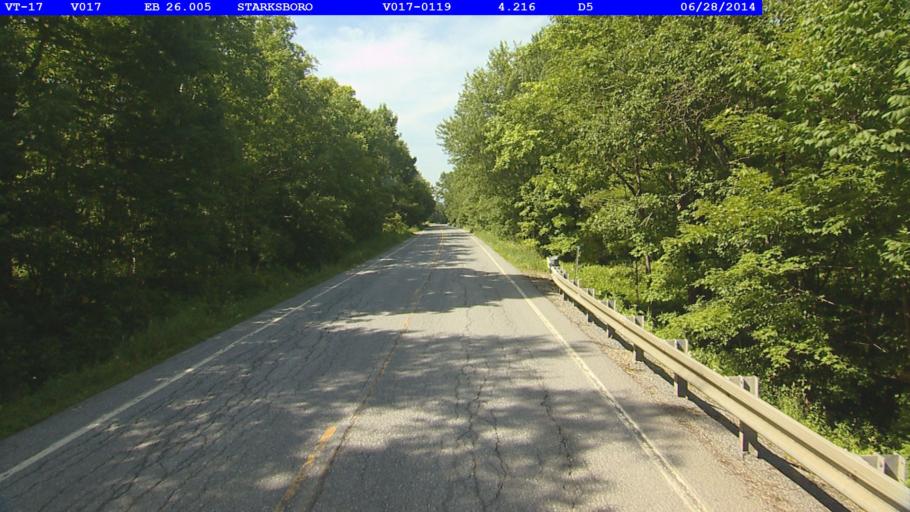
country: US
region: Vermont
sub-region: Addison County
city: Bristol
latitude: 44.1998
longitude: -72.9650
